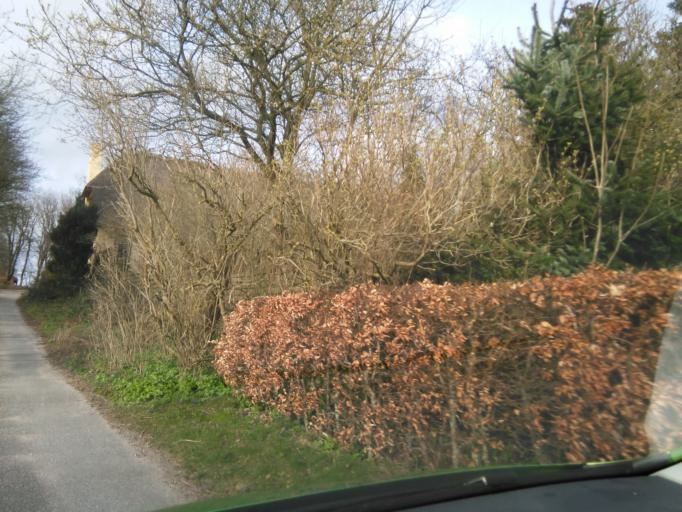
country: DK
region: Central Jutland
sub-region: Arhus Kommune
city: Trige
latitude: 56.2081
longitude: 10.1315
